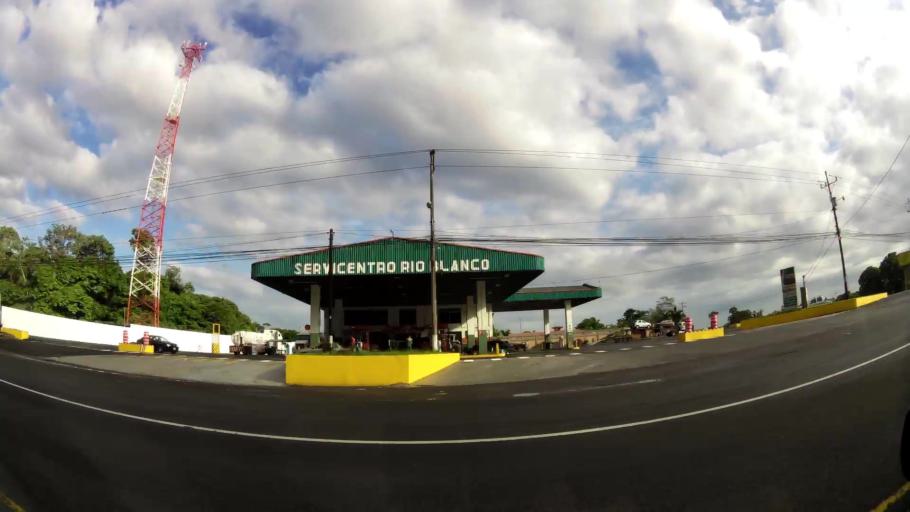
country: CR
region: Limon
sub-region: Canton de Pococi
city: Guapiles
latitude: 10.2127
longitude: -83.8387
